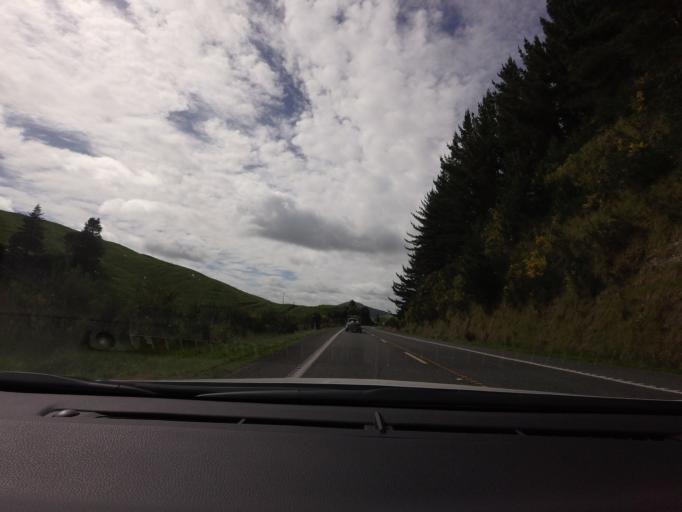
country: NZ
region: Bay of Plenty
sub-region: Rotorua District
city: Rotorua
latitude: -38.2877
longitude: 176.3501
